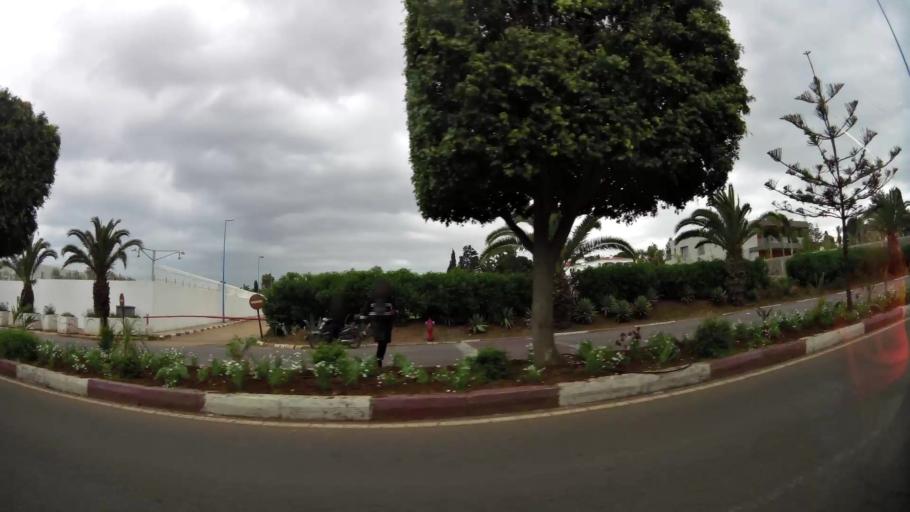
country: MA
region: Grand Casablanca
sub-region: Casablanca
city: Casablanca
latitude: 33.5358
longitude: -7.6302
